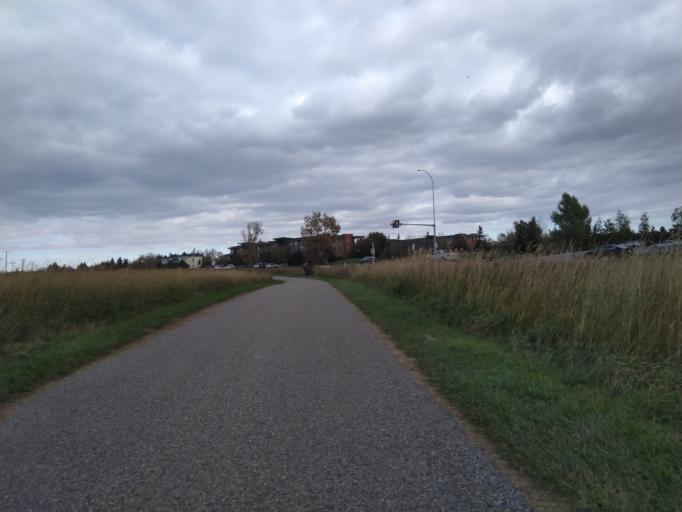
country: CA
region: Alberta
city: Calgary
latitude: 51.0269
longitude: -113.9969
